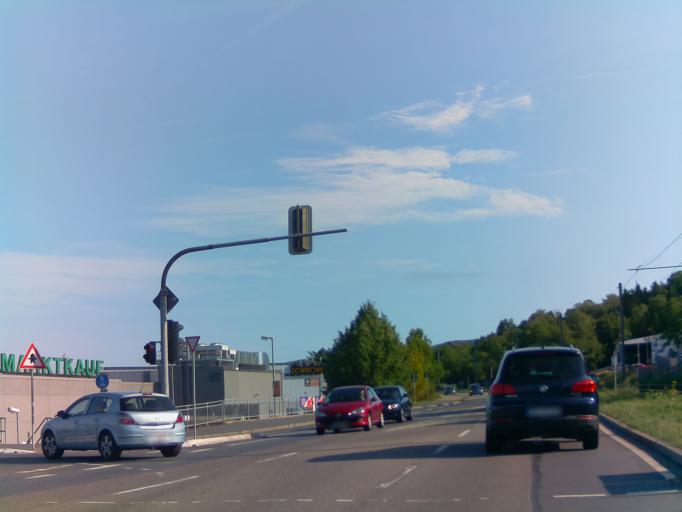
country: DE
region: Baden-Wuerttemberg
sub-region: Karlsruhe Region
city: Weinheim
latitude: 49.5332
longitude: 8.6587
